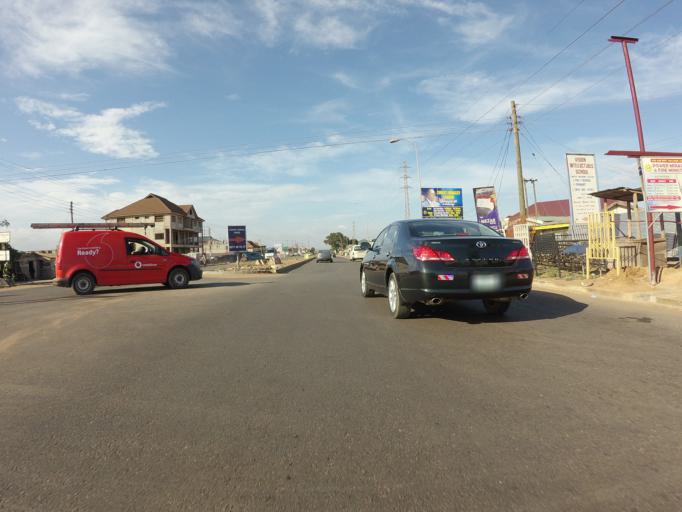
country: GH
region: Greater Accra
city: Nungua
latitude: 5.6372
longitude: -0.0630
